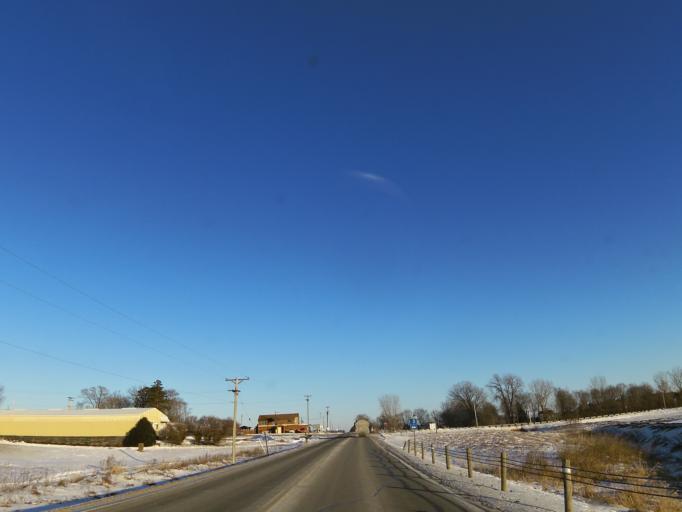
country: US
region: Minnesota
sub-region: Rice County
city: Northfield
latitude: 44.5437
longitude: -93.1386
